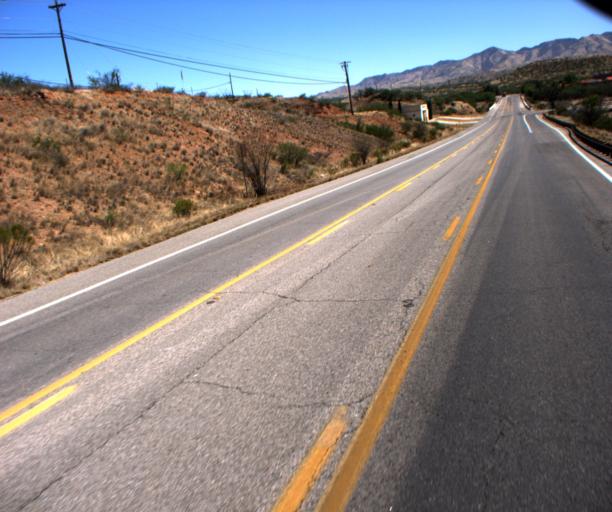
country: US
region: Arizona
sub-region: Santa Cruz County
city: Nogales
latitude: 31.3857
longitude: -110.8775
